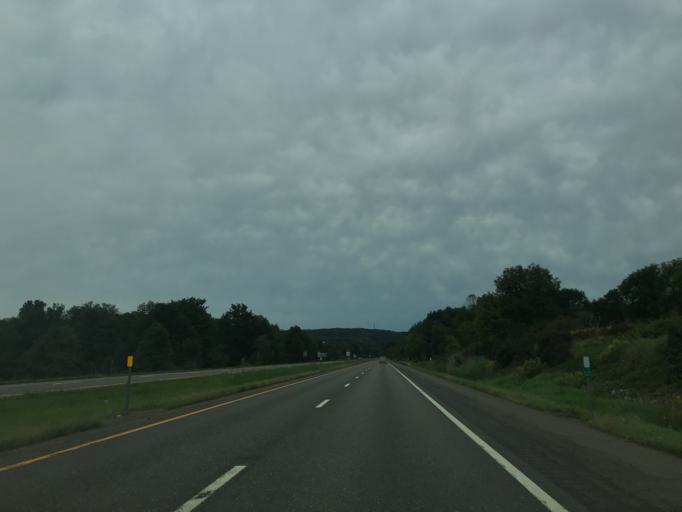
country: US
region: New York
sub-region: Broome County
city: Chenango Bridge
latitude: 42.1623
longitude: -75.8184
